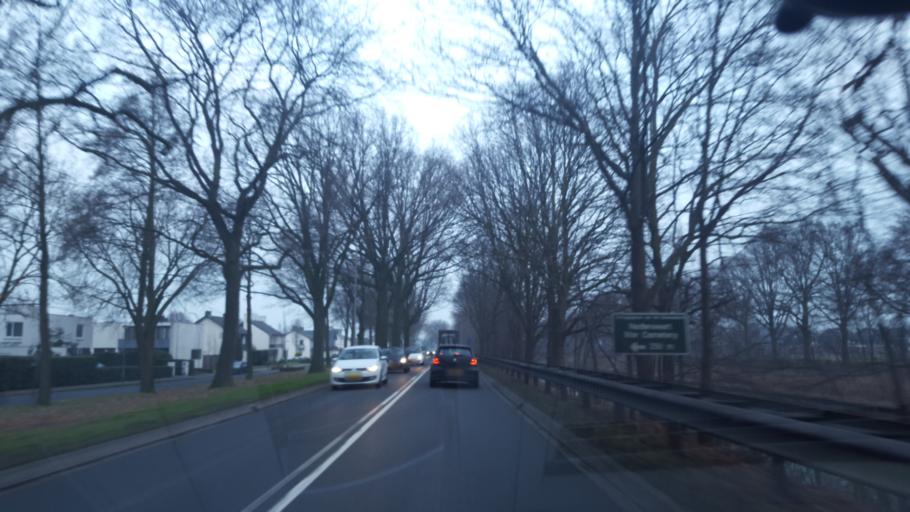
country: NL
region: Limburg
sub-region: Gemeente Nederweert
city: Nederweert
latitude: 51.2879
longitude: 5.7535
